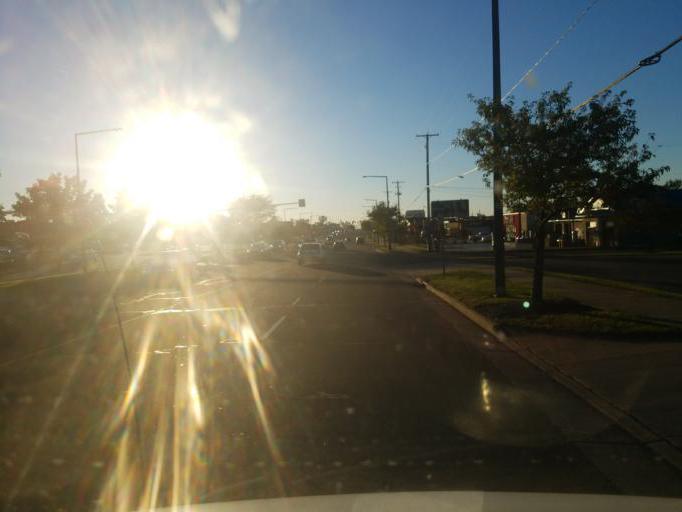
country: US
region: Ohio
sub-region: Stark County
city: Alliance
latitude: 40.9019
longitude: -81.1308
